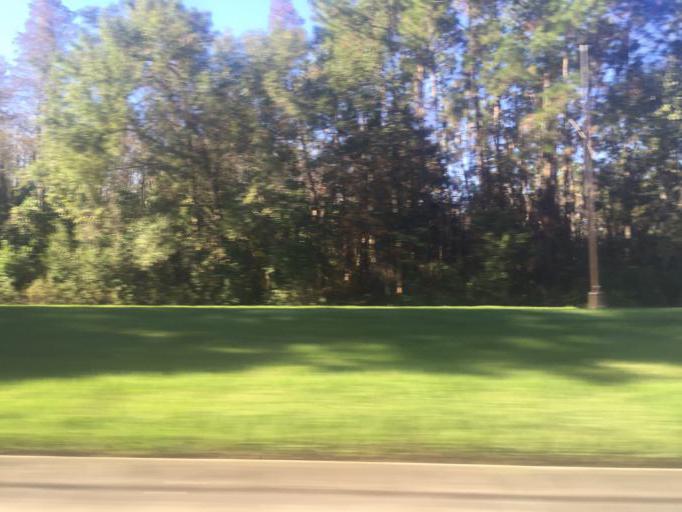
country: US
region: Florida
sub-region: Osceola County
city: Celebration
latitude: 28.3966
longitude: -81.5724
